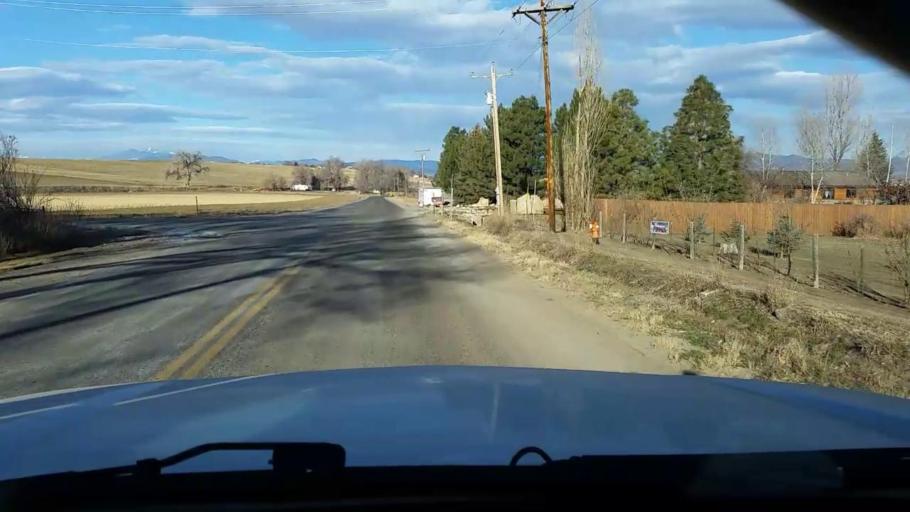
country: US
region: Colorado
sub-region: Larimer County
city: Campion
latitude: 40.3712
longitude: -105.0592
